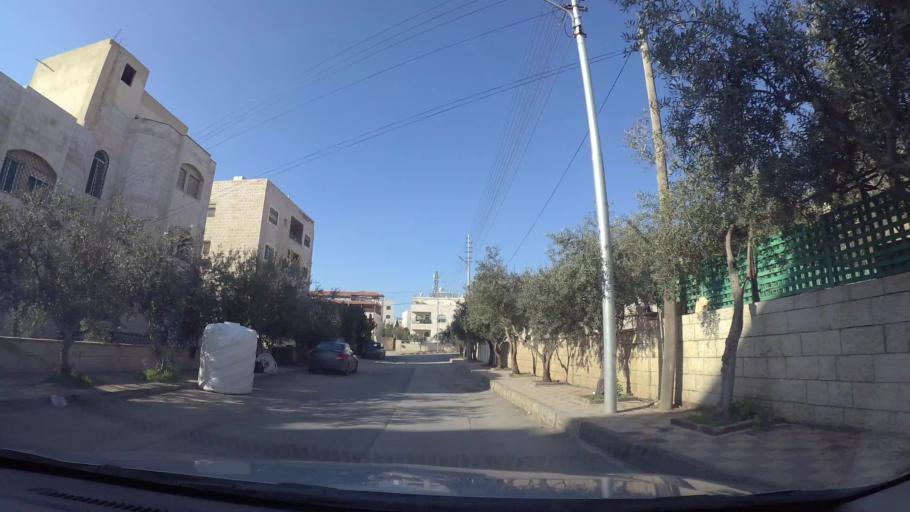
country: JO
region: Amman
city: Al Bunayyat ash Shamaliyah
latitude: 31.8980
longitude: 35.9196
